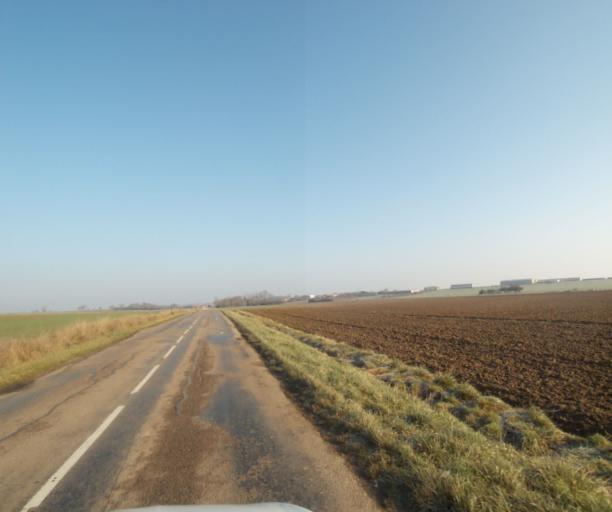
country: FR
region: Champagne-Ardenne
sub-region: Departement de la Haute-Marne
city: Montier-en-Der
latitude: 48.4452
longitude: 4.7605
